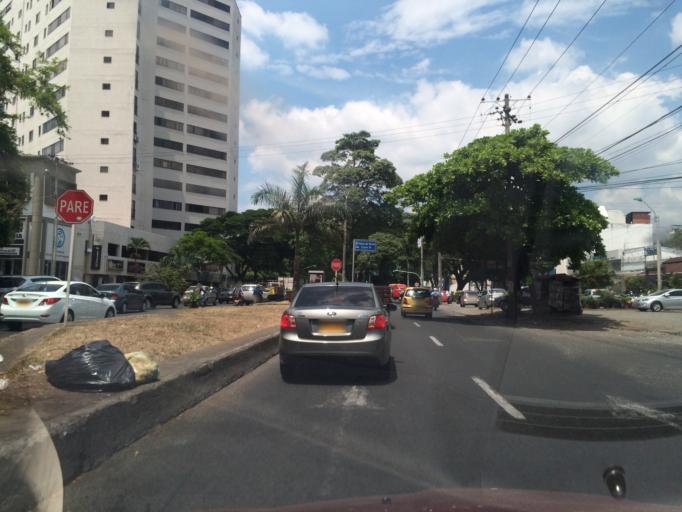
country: CO
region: Valle del Cauca
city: Cali
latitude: 3.4210
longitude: -76.5423
